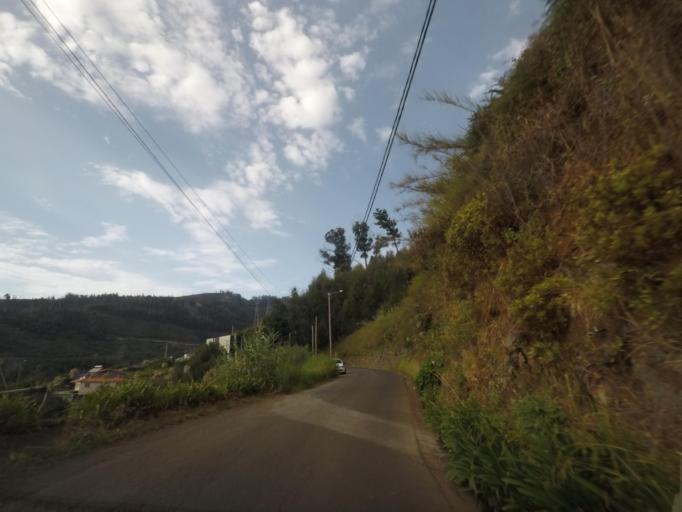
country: PT
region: Madeira
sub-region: Calheta
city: Arco da Calheta
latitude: 32.7356
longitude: -17.1538
